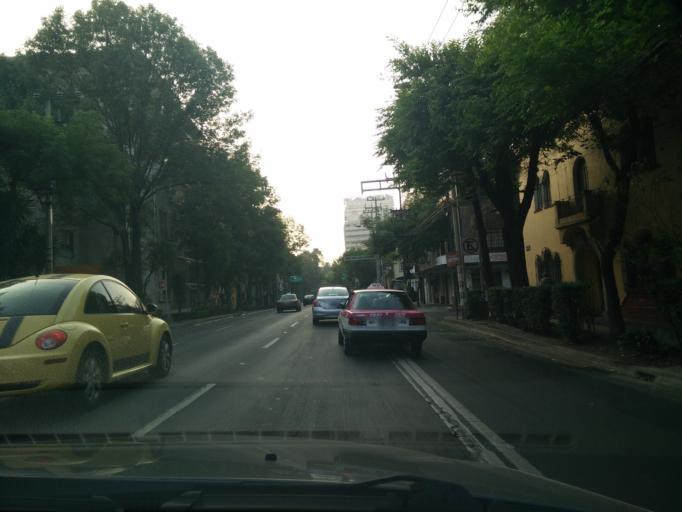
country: MX
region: Mexico City
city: Benito Juarez
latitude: 19.4148
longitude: -99.1748
